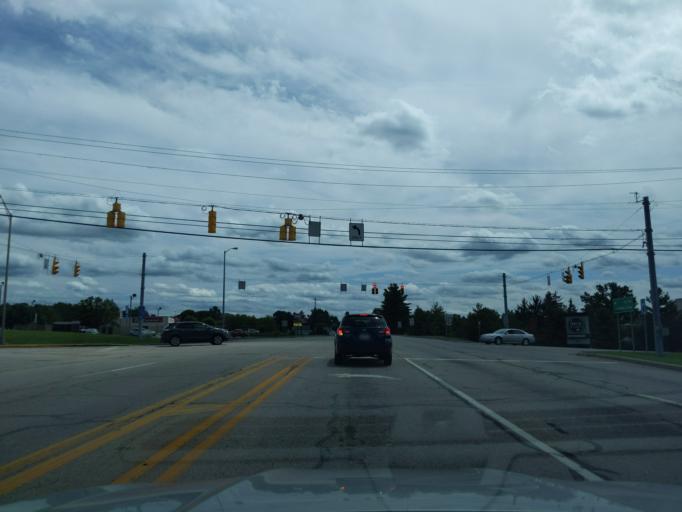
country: US
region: Indiana
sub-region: Ripley County
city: Batesville
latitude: 39.3063
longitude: -85.2185
